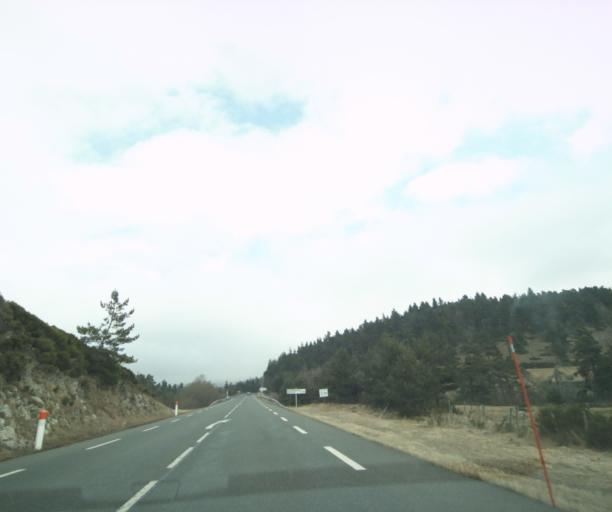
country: FR
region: Languedoc-Roussillon
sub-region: Departement de la Lozere
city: Langogne
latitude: 44.6527
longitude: 3.7337
